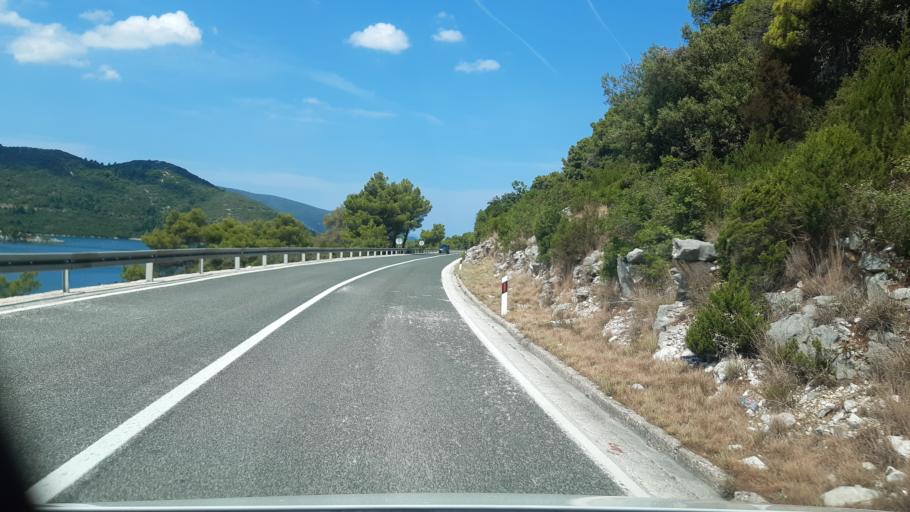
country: HR
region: Dubrovacko-Neretvanska
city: Ston
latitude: 42.8679
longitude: 17.6934
